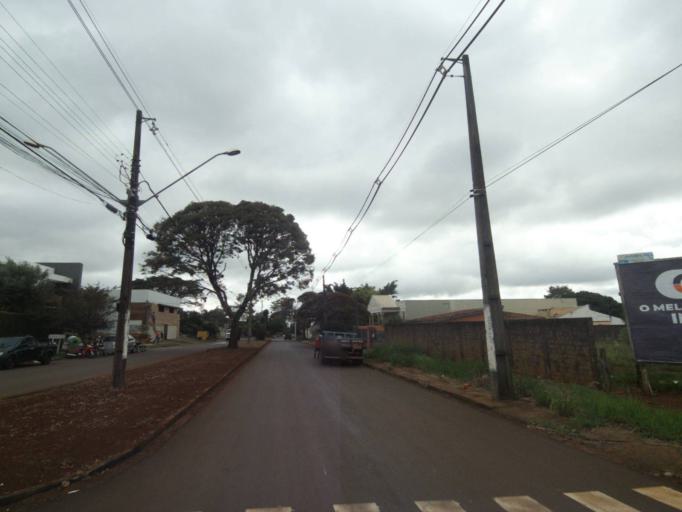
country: BR
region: Parana
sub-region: Campo Mourao
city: Campo Mourao
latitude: -24.0418
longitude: -52.3674
